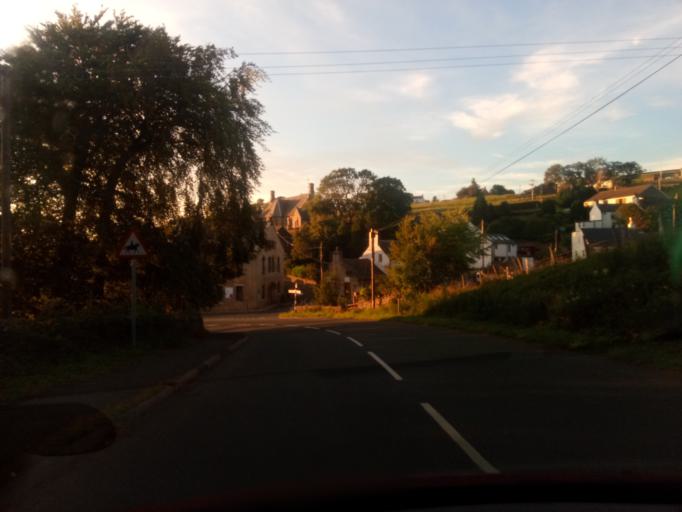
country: GB
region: England
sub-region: Northumberland
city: Bardon Mill
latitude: 54.7872
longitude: -2.3414
